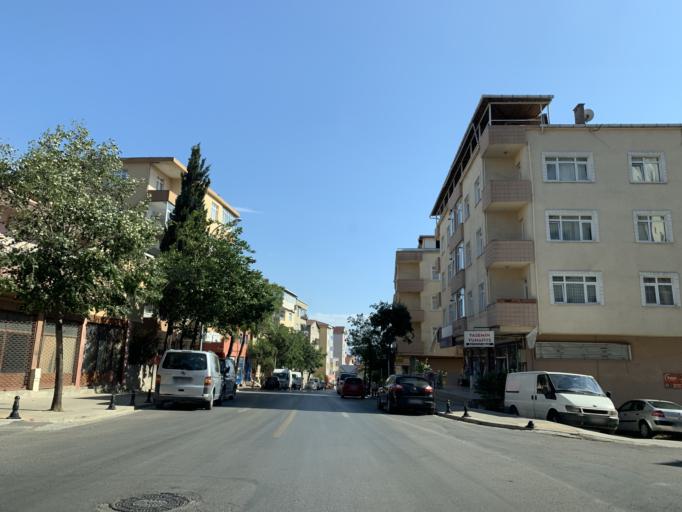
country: TR
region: Istanbul
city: Pendik
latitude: 40.8768
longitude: 29.2805
